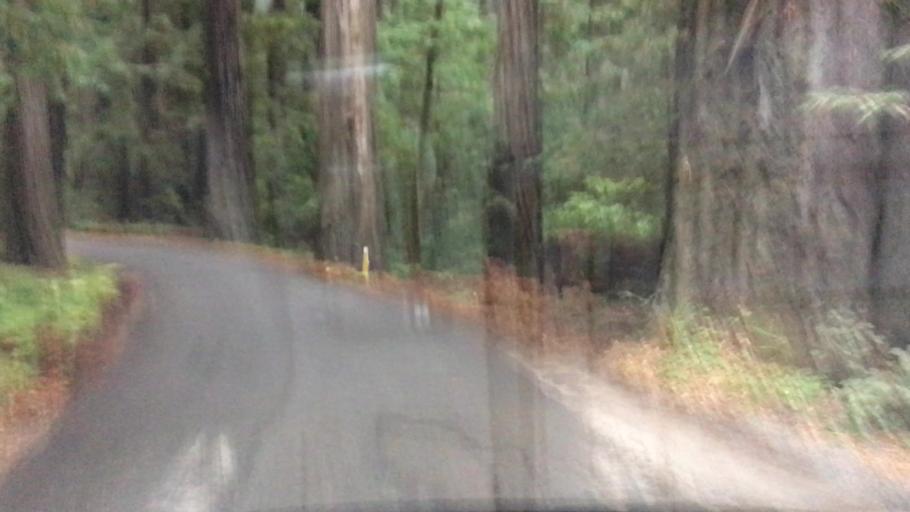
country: US
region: California
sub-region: Humboldt County
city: Rio Dell
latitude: 40.3524
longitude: -123.9782
